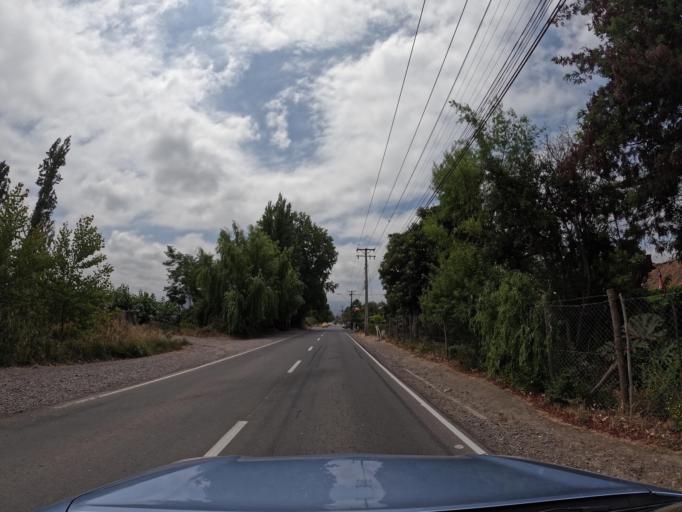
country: CL
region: O'Higgins
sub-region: Provincia de Colchagua
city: Chimbarongo
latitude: -34.7308
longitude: -70.9903
